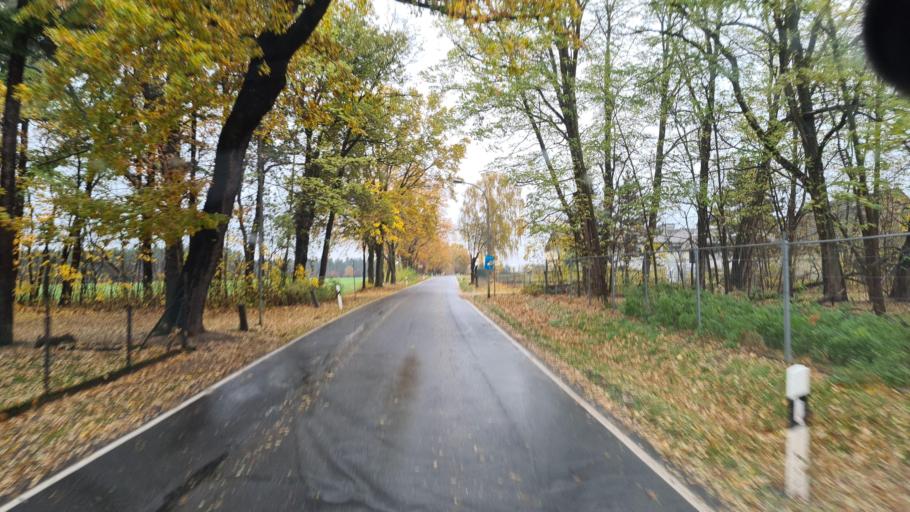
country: DE
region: Brandenburg
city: Drebkau
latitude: 51.6831
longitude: 14.2041
